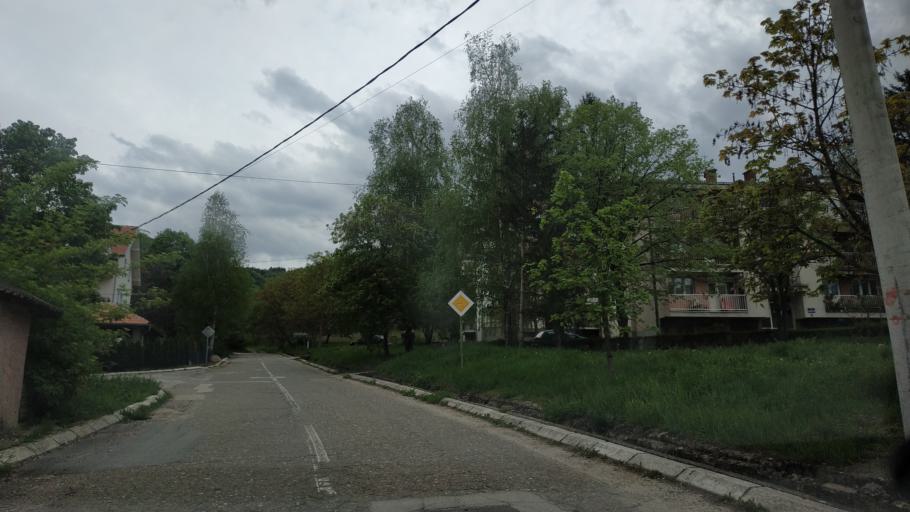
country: RS
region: Central Serbia
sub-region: Zajecarski Okrug
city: Soko Banja
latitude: 43.6413
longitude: 21.8652
